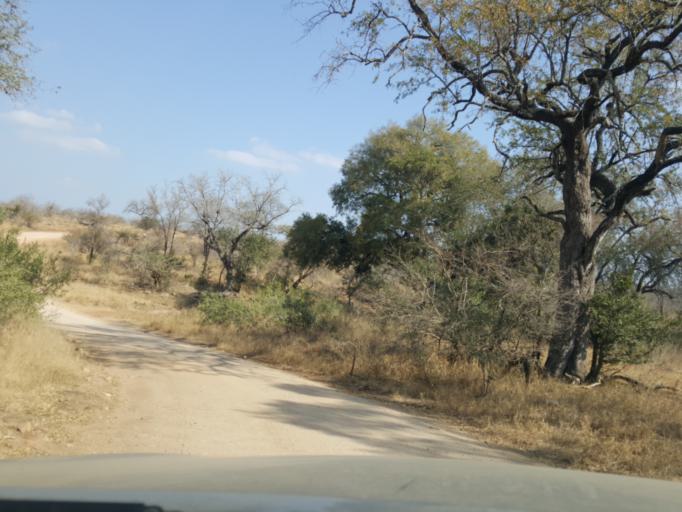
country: ZA
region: Mpumalanga
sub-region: Ehlanzeni District
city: Komatipoort
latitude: -25.2909
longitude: 31.7639
